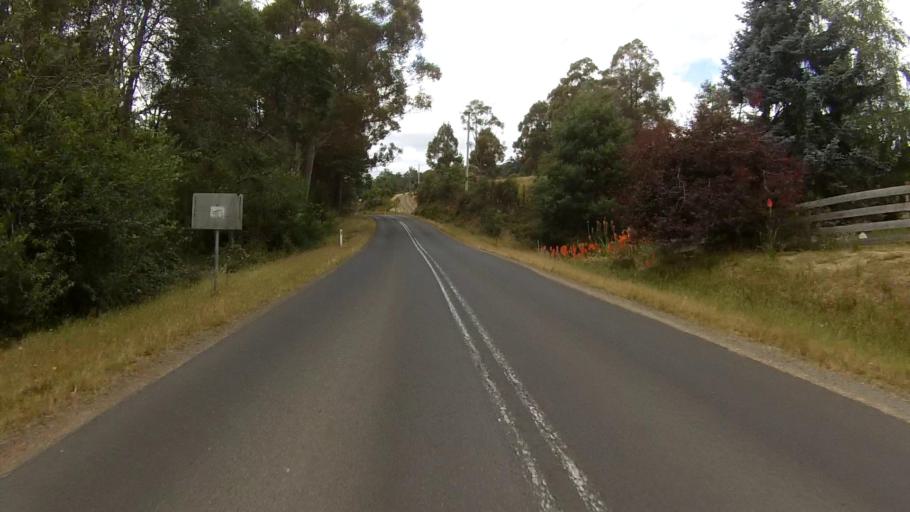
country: AU
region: Tasmania
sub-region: Huon Valley
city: Cygnet
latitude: -43.1482
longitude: 147.1526
